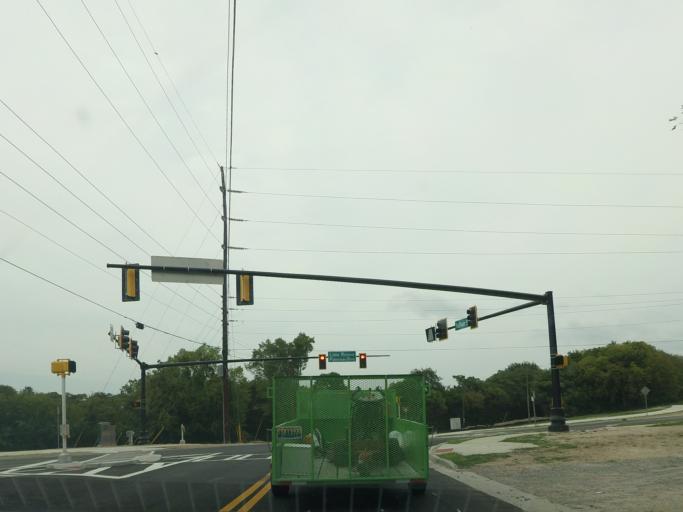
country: US
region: Georgia
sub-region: Bibb County
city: Macon
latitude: 32.8252
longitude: -83.6426
